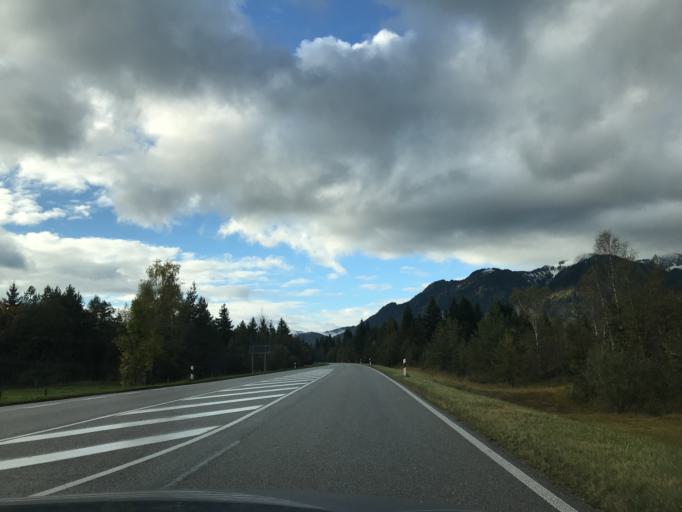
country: DE
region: Bavaria
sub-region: Upper Bavaria
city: Lenggries
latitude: 47.7051
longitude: 11.5621
